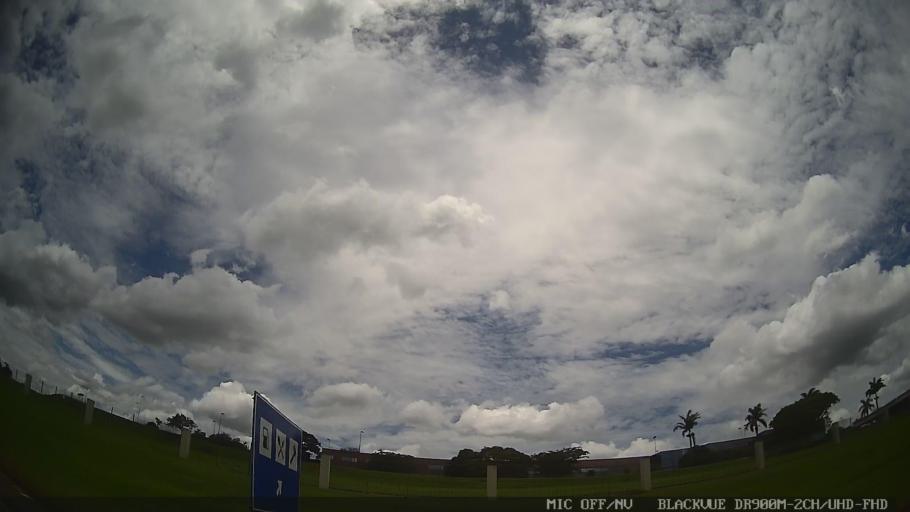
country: BR
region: Sao Paulo
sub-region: Jaguariuna
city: Jaguariuna
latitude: -22.7233
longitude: -47.0140
